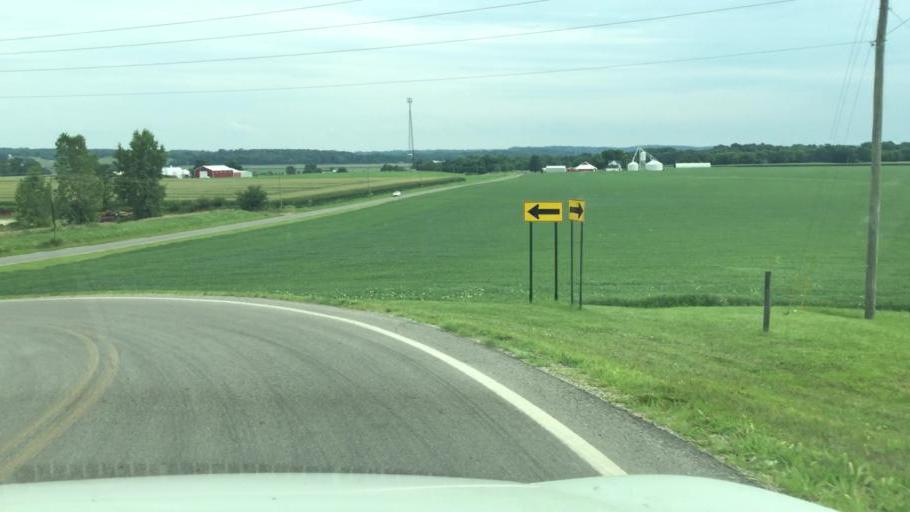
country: US
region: Ohio
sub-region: Champaign County
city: Mechanicsburg
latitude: 40.0401
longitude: -83.6562
